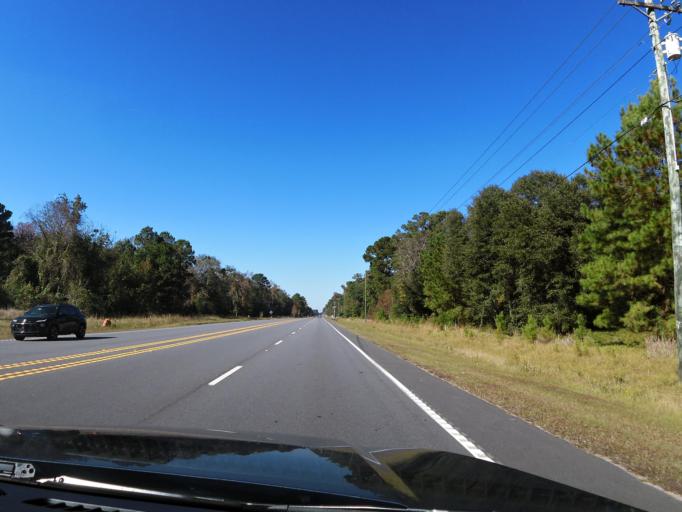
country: US
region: Georgia
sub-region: Liberty County
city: Midway
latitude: 31.7823
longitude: -81.3857
